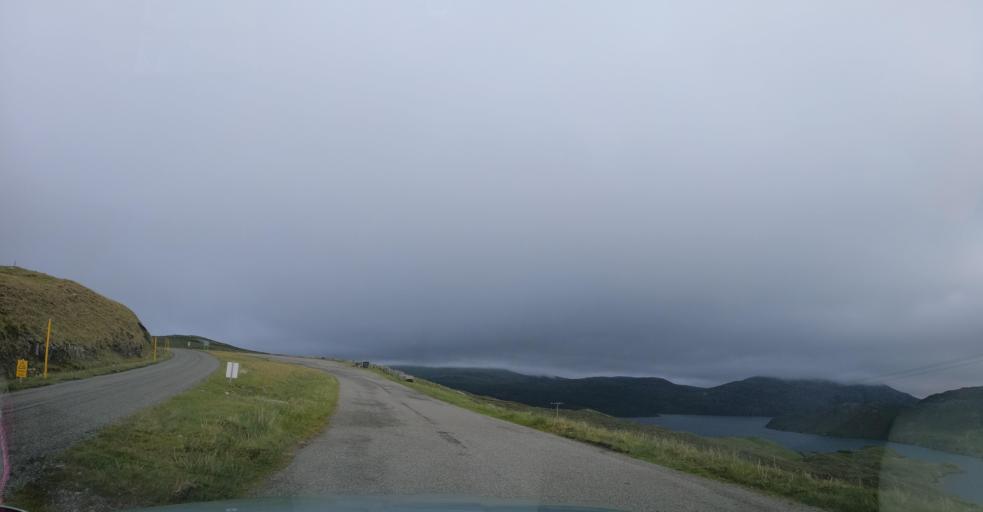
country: GB
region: Scotland
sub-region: Eilean Siar
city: Harris
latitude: 57.9593
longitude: -6.7465
